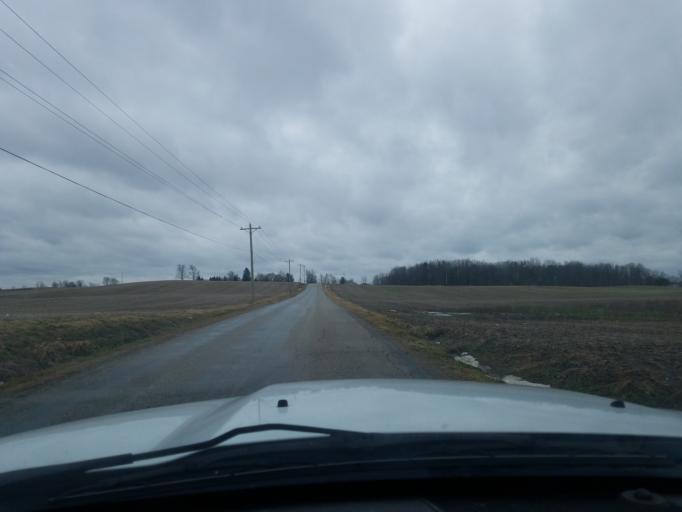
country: US
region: Indiana
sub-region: Noble County
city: Albion
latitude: 41.4279
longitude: -85.3954
